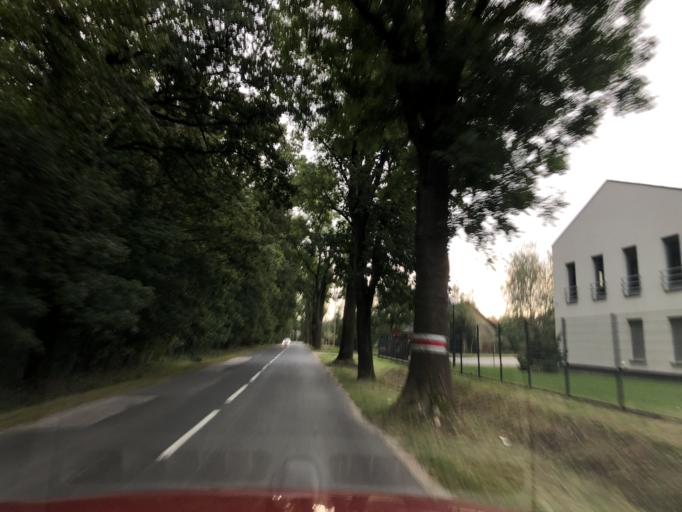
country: PL
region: Lower Silesian Voivodeship
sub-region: Powiat wroclawski
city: Dlugoleka
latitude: 51.1890
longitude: 17.1847
